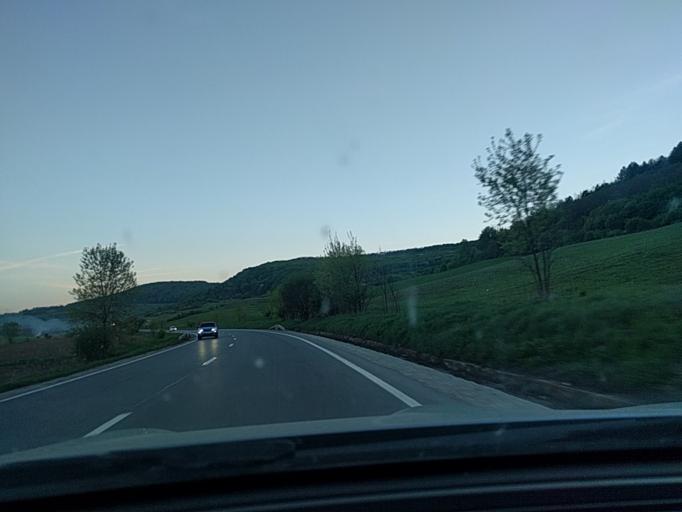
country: RO
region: Mures
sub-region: Comuna Nades
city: Nades
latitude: 46.3071
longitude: 24.7199
